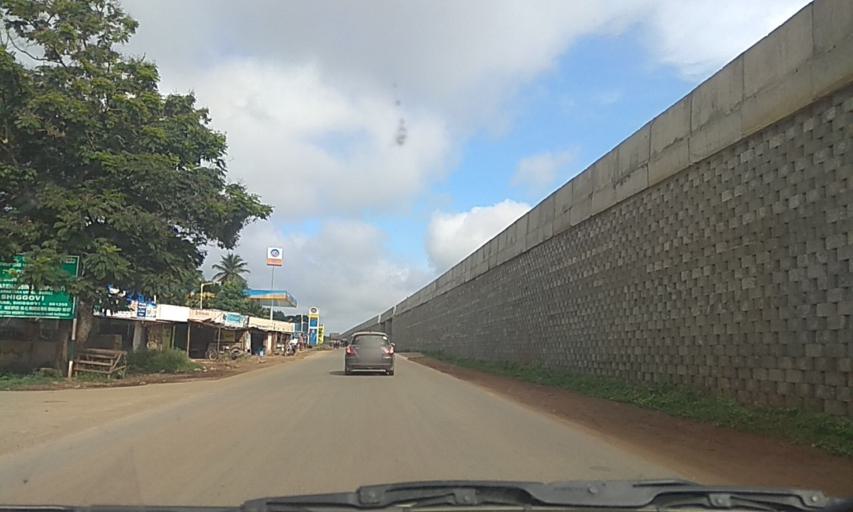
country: IN
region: Karnataka
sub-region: Haveri
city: Shiggaon
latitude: 14.9925
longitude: 75.2157
